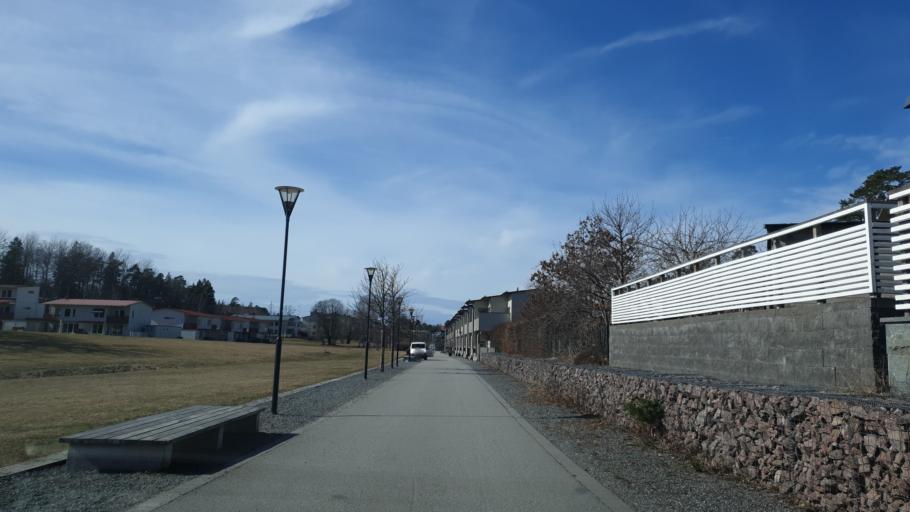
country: SE
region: Stockholm
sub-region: Solna Kommun
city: Rasunda
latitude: 59.4000
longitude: 17.9958
